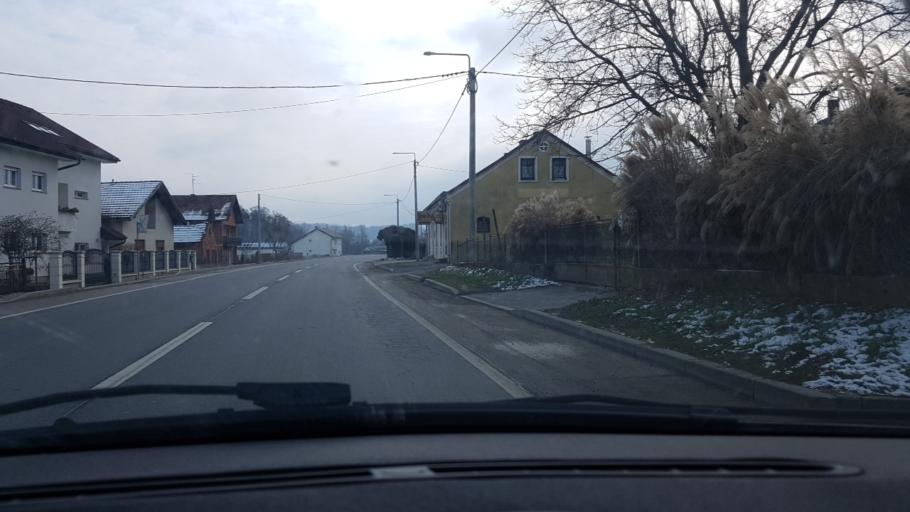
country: HR
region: Varazdinska
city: Tuzno
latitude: 46.2745
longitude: 16.2078
